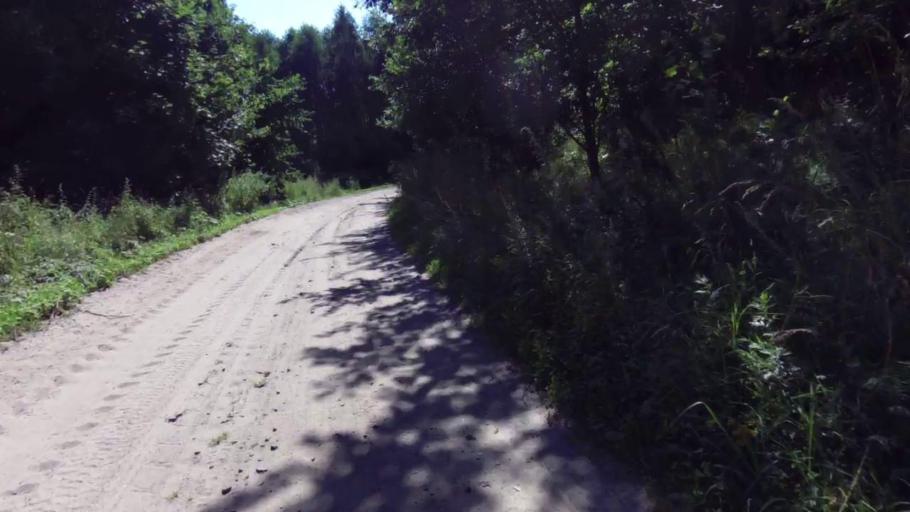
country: PL
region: West Pomeranian Voivodeship
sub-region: Powiat drawski
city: Zlocieniec
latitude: 53.5212
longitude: 16.0478
